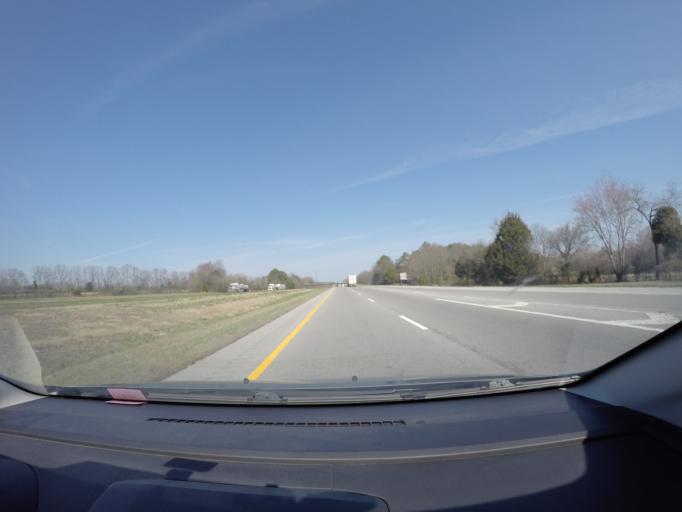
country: US
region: Tennessee
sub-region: Coffee County
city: Manchester
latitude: 35.3953
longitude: -85.9937
